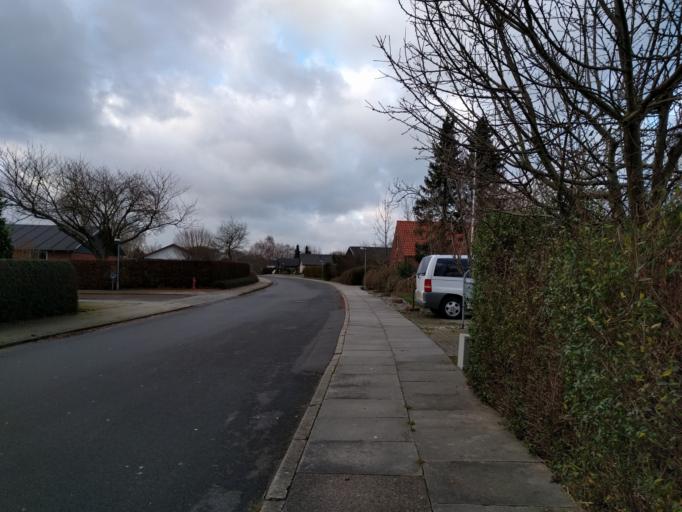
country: DK
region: Central Jutland
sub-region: Silkeborg Kommune
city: Silkeborg
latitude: 56.1913
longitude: 9.5236
